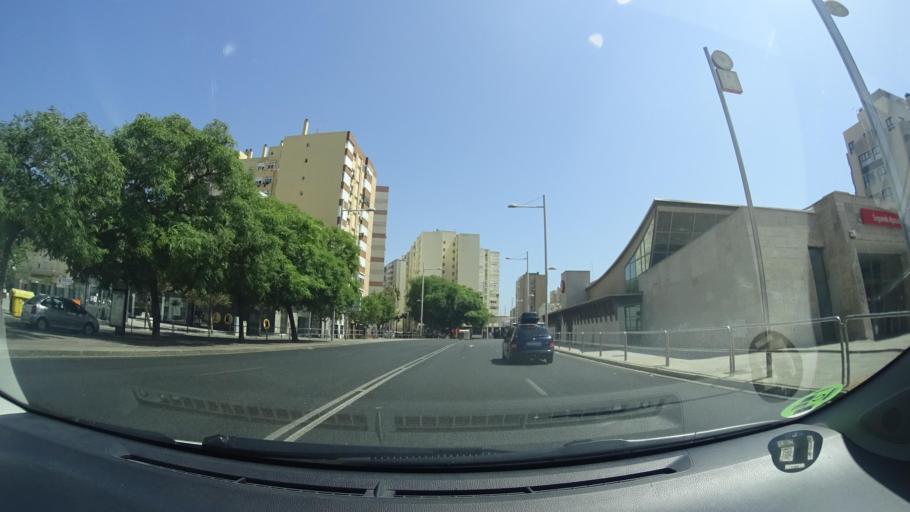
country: ES
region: Andalusia
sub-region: Provincia de Cadiz
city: Cadiz
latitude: 36.5140
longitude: -6.2770
